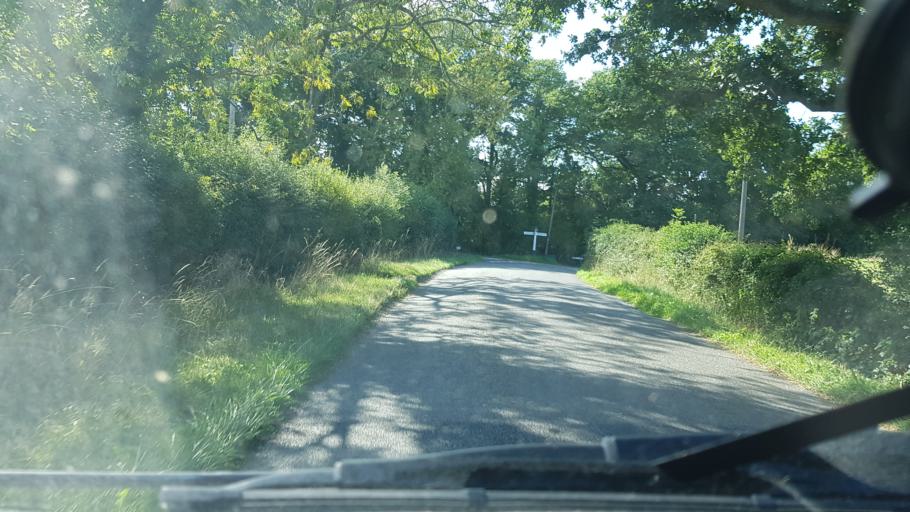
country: GB
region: England
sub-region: West Sussex
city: Horsham
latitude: 51.0952
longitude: -0.3519
